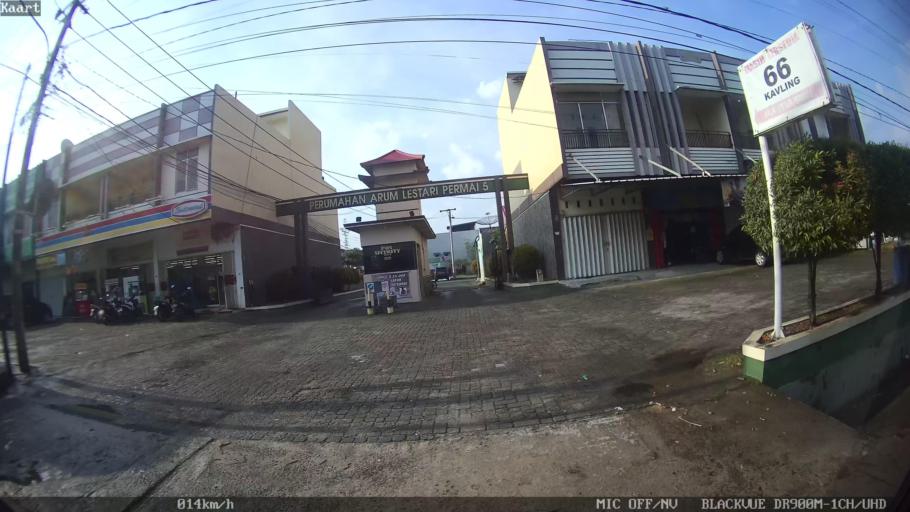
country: ID
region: Lampung
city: Kedaton
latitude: -5.3857
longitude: 105.3148
